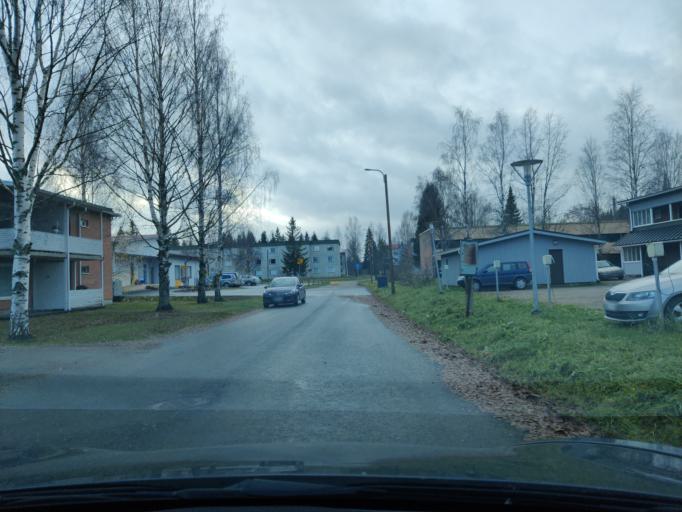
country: FI
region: Northern Savo
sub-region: Ylae-Savo
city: Kiuruvesi
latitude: 63.6468
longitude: 26.6340
